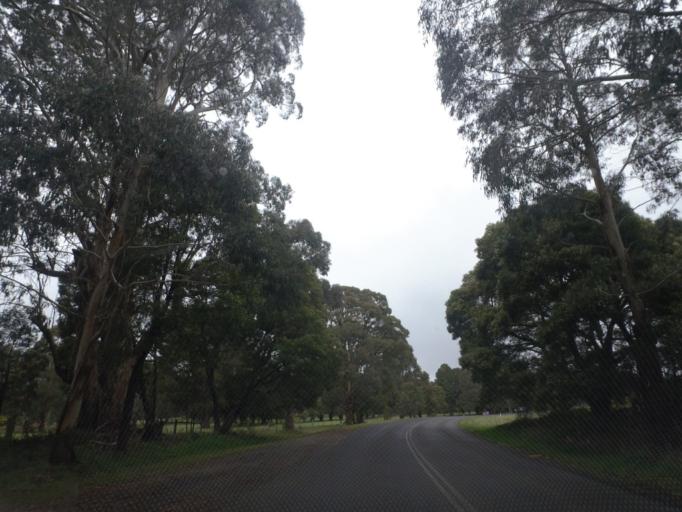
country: AU
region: Victoria
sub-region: Moorabool
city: Bacchus Marsh
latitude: -37.3744
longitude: 144.3178
